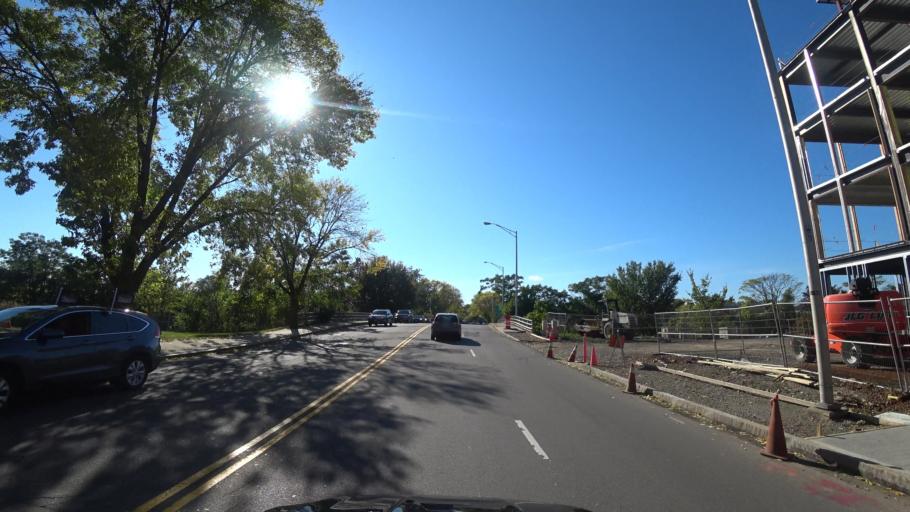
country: US
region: Massachusetts
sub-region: Middlesex County
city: Malden
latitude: 42.4180
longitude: -71.0721
